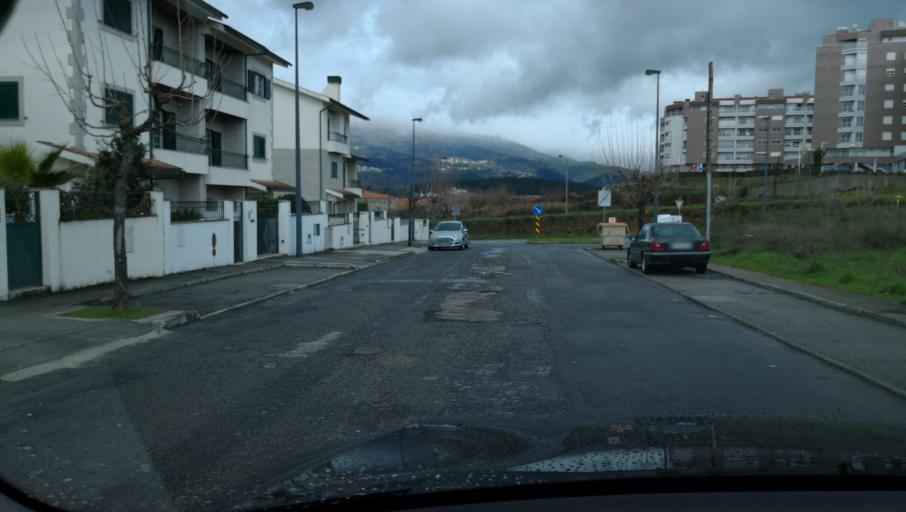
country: PT
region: Vila Real
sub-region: Vila Real
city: Vila Real
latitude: 41.3046
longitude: -7.7227
